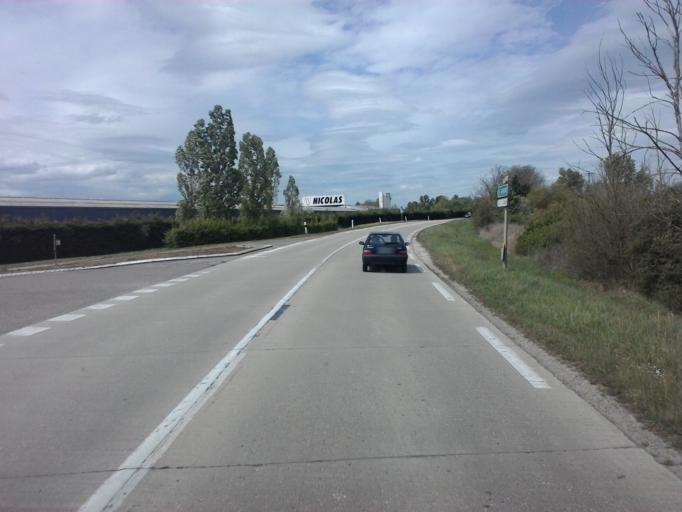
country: FR
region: Bourgogne
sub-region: Departement de l'Yonne
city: Champs-sur-Yonne
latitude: 47.7420
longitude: 3.6039
